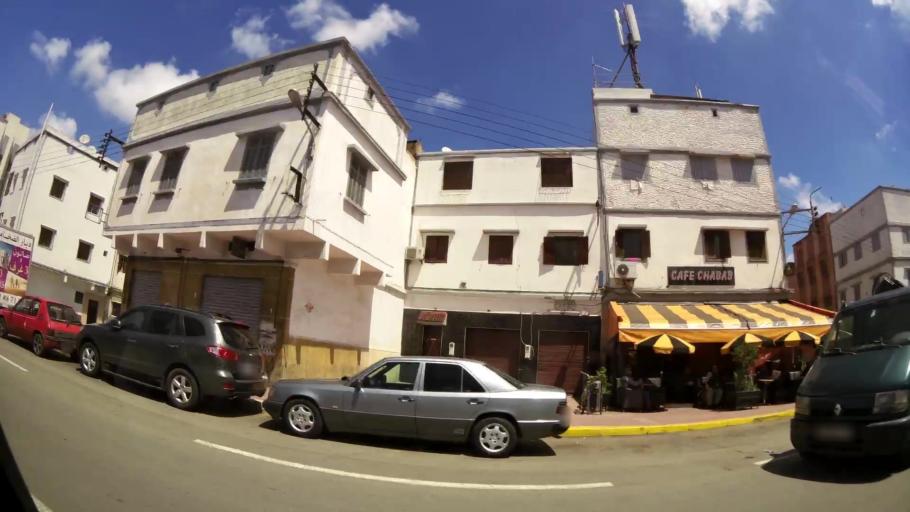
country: MA
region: Grand Casablanca
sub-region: Casablanca
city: Casablanca
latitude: 33.5618
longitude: -7.5658
